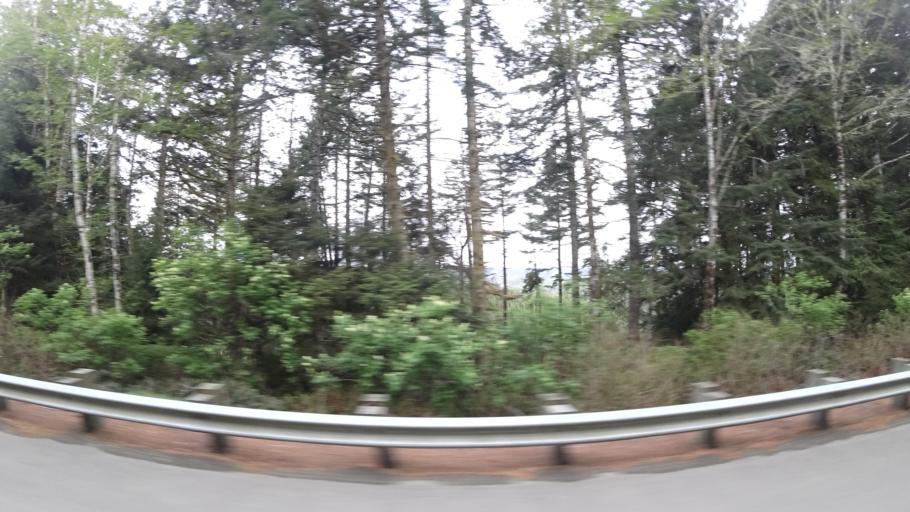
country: US
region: Oregon
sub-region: Coos County
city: Barview
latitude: 43.2463
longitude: -124.2873
